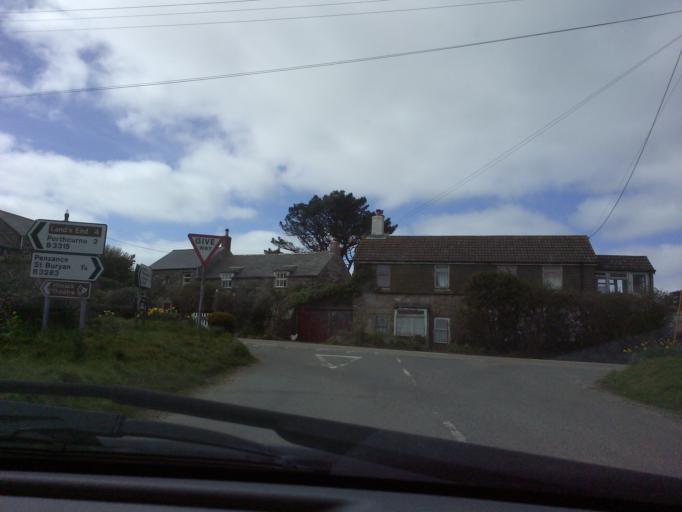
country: GB
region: England
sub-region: Cornwall
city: St. Buryan
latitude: 50.0599
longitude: -5.6360
